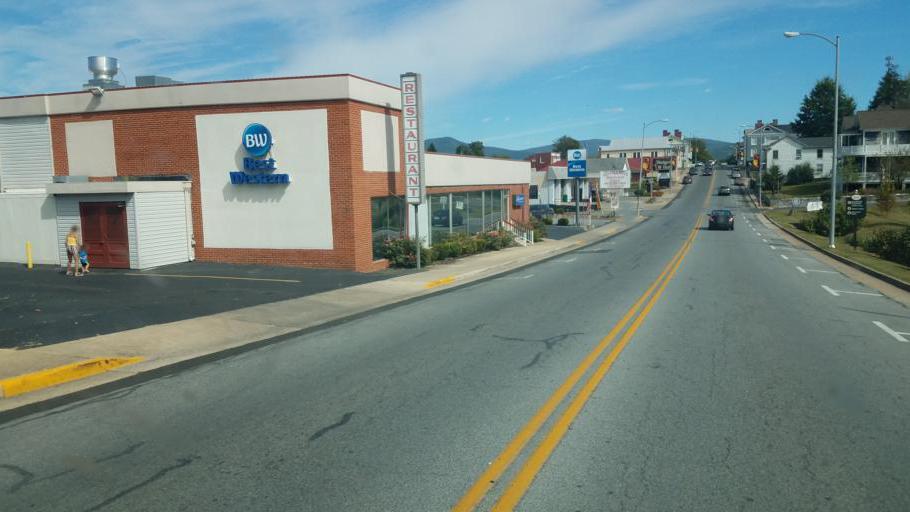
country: US
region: Virginia
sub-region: Page County
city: Luray
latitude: 38.6656
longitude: -78.4673
